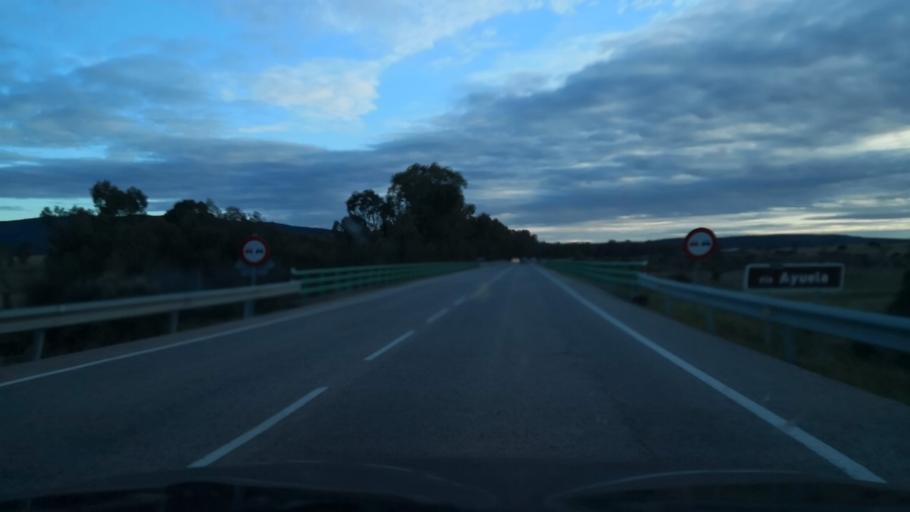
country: ES
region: Extremadura
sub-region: Provincia de Caceres
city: Malpartida de Caceres
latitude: 39.3336
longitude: -6.4842
